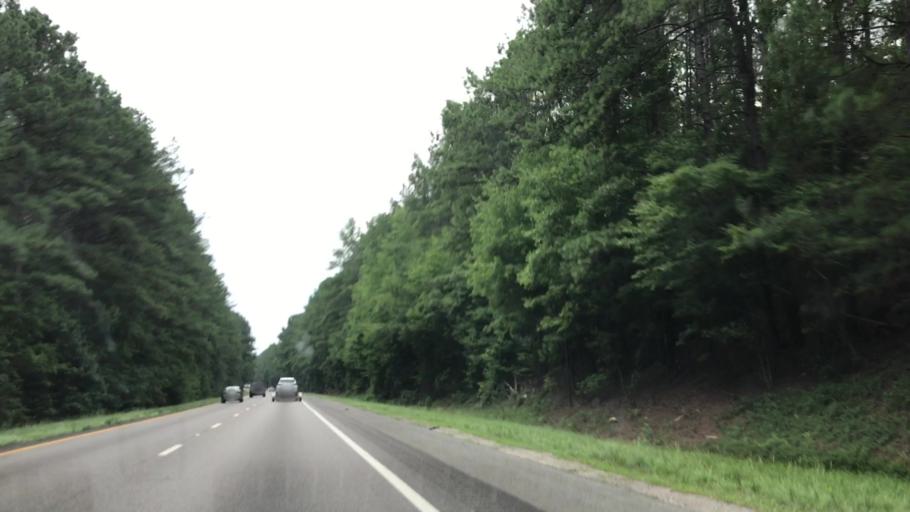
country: US
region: South Carolina
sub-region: Richland County
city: Blythewood
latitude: 34.2591
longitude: -80.9989
